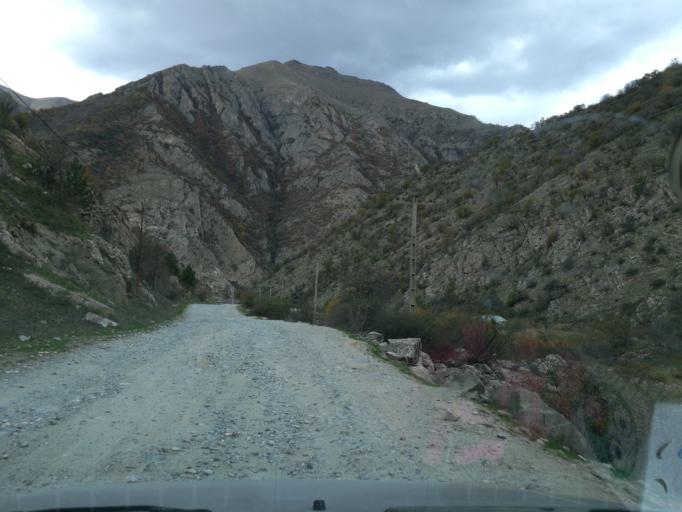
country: IR
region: Mazandaran
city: `Abbasabad
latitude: 36.4403
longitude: 51.0673
